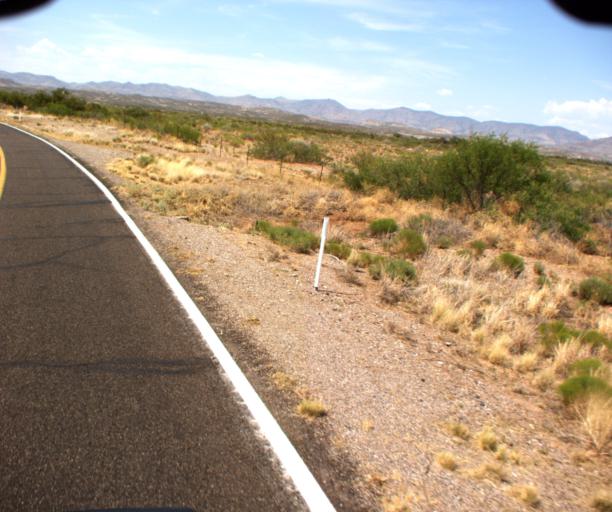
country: US
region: Arizona
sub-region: Greenlee County
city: Clifton
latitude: 32.9638
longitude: -109.2062
